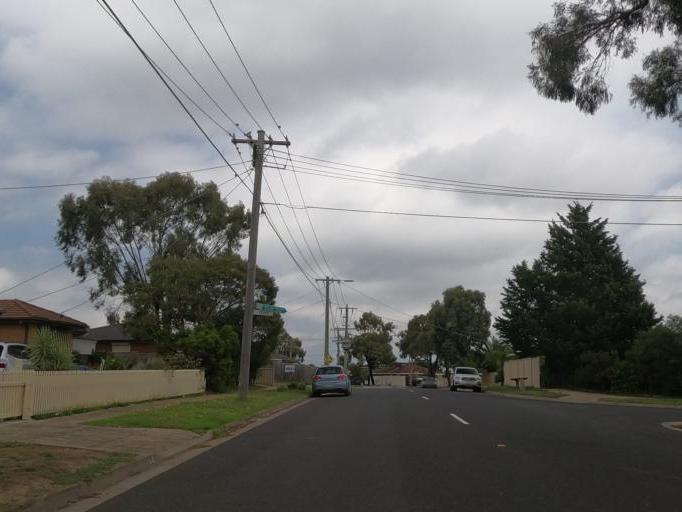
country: AU
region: Victoria
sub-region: Hume
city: Westmeadows
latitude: -37.6725
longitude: 144.8985
